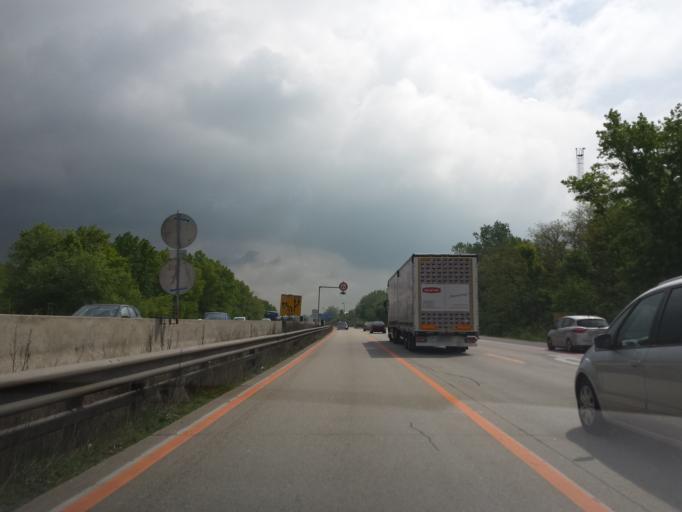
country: AT
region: Lower Austria
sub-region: Politischer Bezirk Wien-Umgebung
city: Rauchenwarth
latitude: 48.1321
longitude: 16.5388
